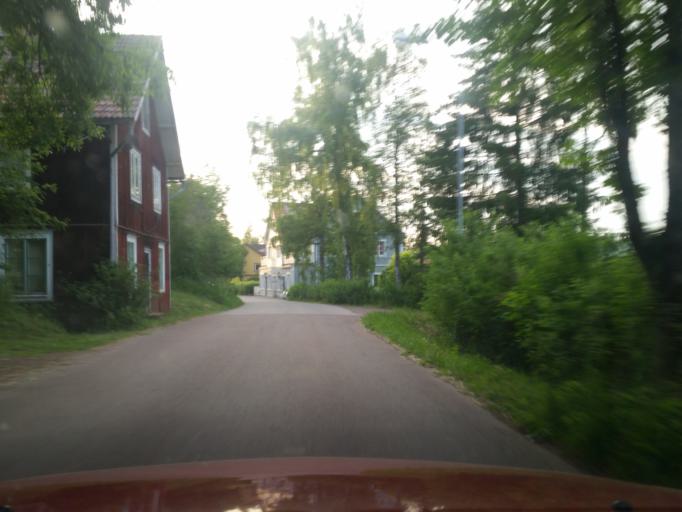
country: SE
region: Dalarna
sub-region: Leksand Municipality
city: Smedby
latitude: 60.6787
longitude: 15.1033
